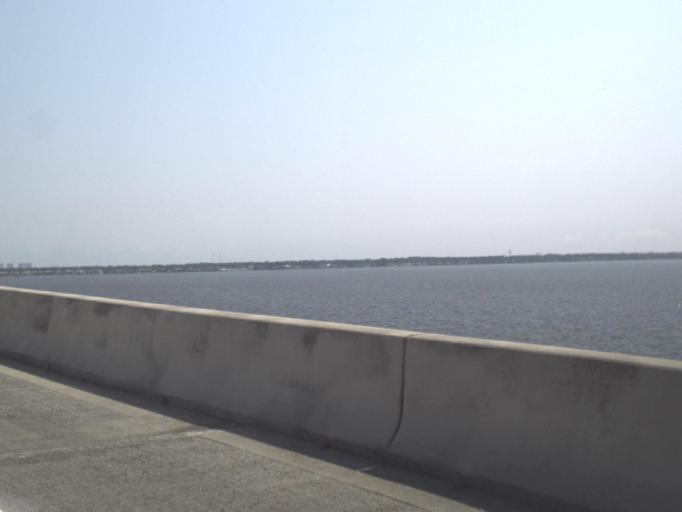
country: US
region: Florida
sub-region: Santa Rosa County
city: Oriole Beach
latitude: 30.4203
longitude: -87.0903
